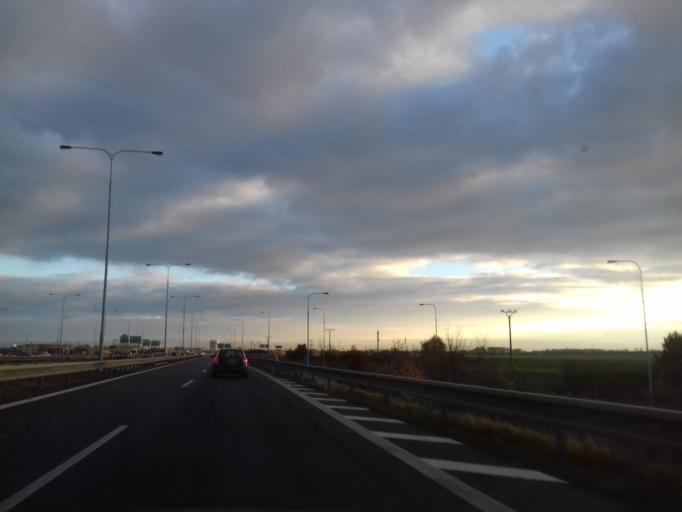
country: CZ
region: Olomoucky
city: Hnevotin
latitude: 49.5629
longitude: 17.2017
